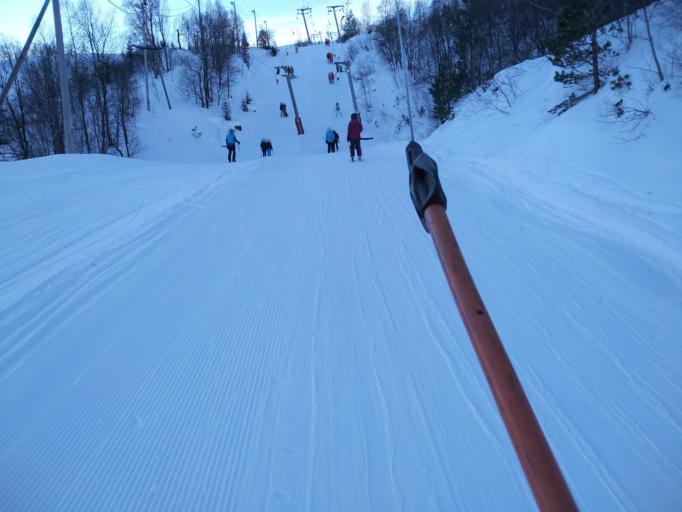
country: NO
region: Rogaland
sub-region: Sauda
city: Sauda
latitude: 59.6224
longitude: 6.2405
